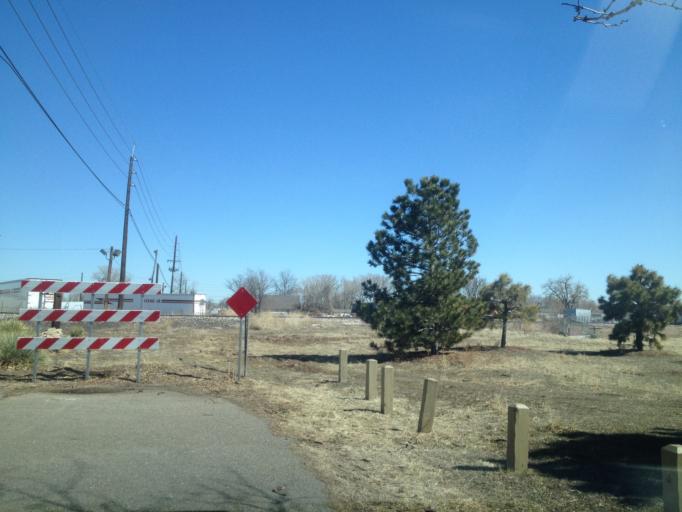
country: US
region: Colorado
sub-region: Adams County
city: Twin Lakes
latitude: 39.7856
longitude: -104.9823
